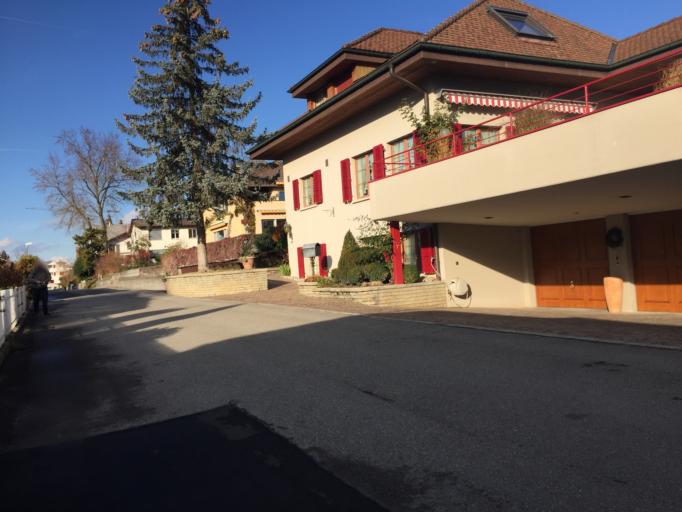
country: CH
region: Bern
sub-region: Bern-Mittelland District
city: Munsingen
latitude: 46.8721
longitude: 7.5699
